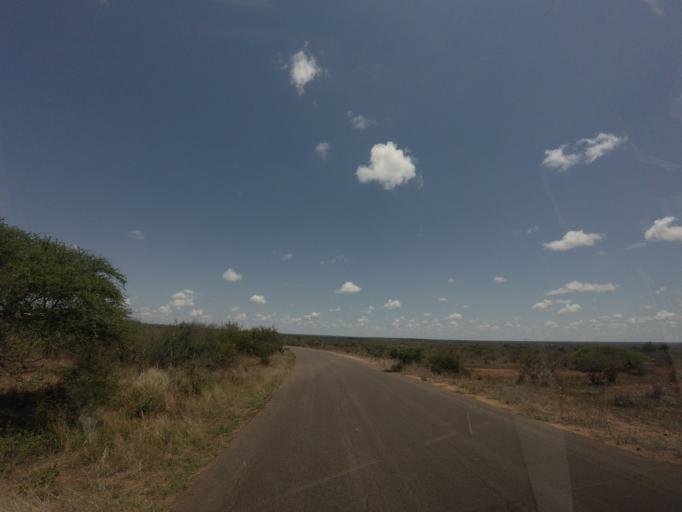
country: ZA
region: Mpumalanga
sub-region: Ehlanzeni District
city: Komatipoort
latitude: -24.8249
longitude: 31.8912
